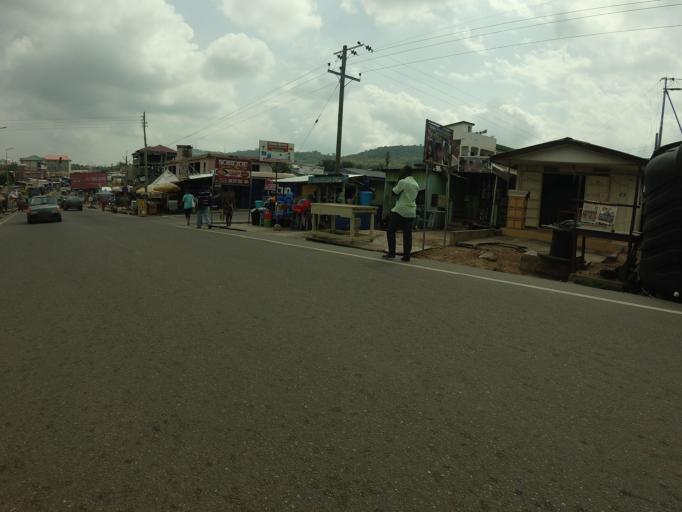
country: GH
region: Volta
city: Ho
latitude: 6.6192
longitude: 0.4706
